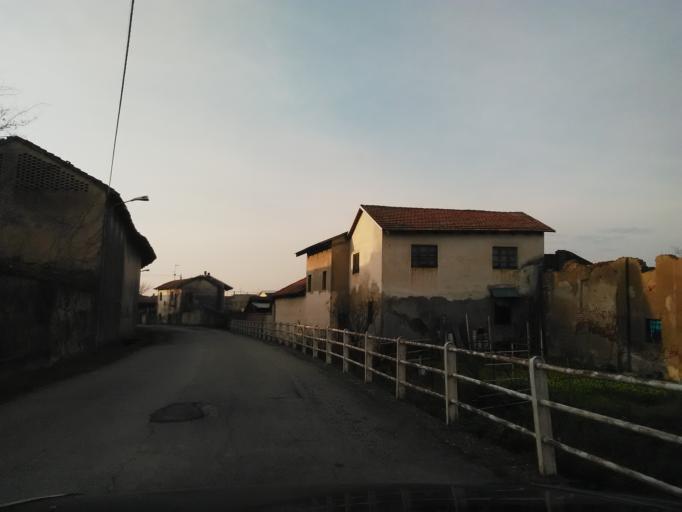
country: IT
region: Piedmont
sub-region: Provincia di Vercelli
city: Olcenengo
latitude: 45.3467
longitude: 8.2942
